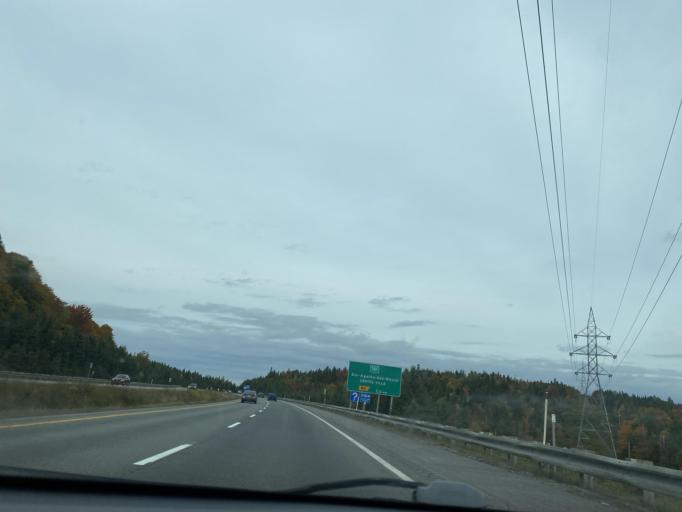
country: CA
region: Quebec
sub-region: Laurentides
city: Sainte-Agathe-des-Monts
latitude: 46.0310
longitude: -74.2643
